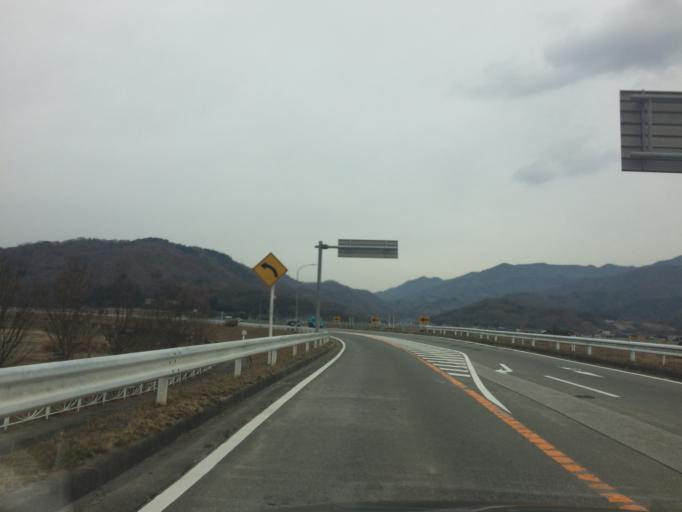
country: JP
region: Yamanashi
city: Ryuo
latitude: 35.4861
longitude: 138.4527
